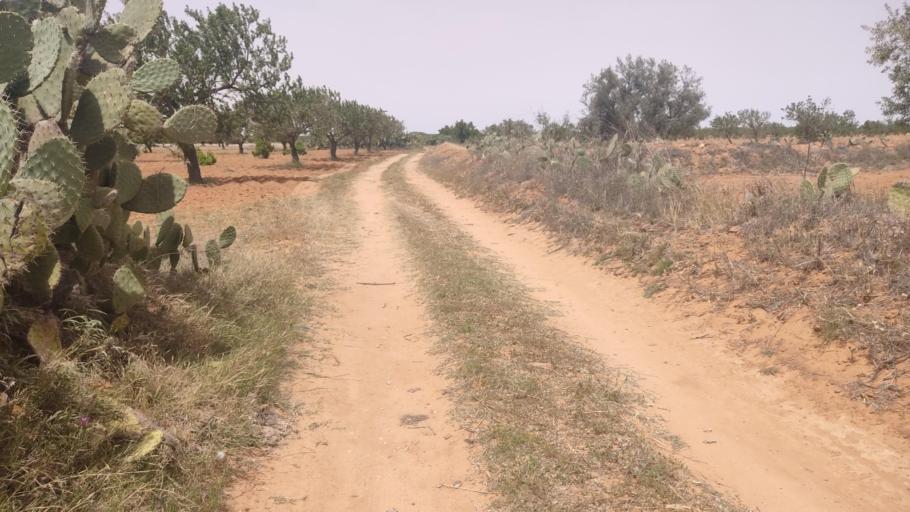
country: TN
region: Safaqis
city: Sfax
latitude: 34.8473
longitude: 10.5953
